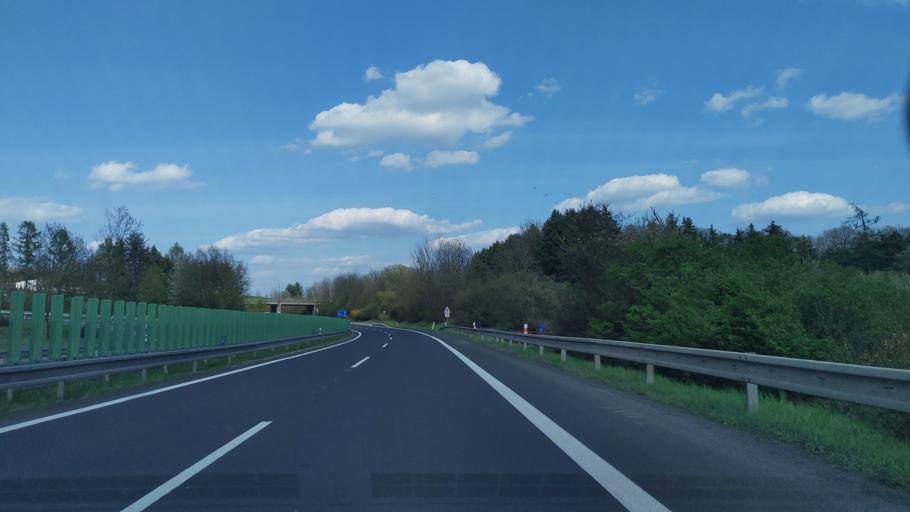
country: CZ
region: Ustecky
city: Hostomice
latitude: 50.6104
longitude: 13.8266
